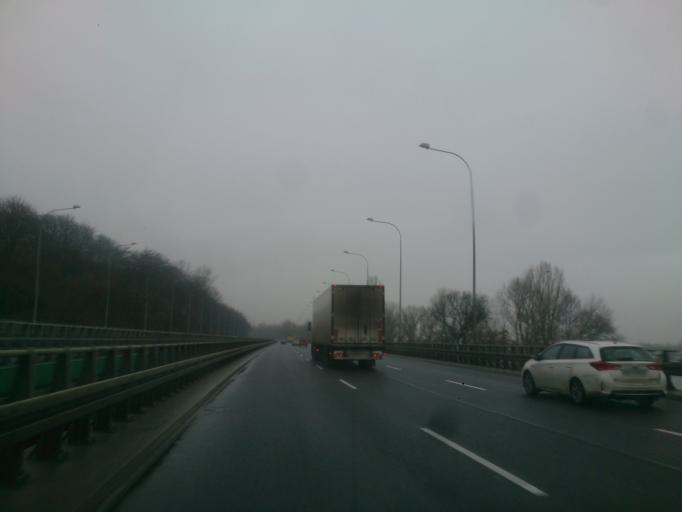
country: PL
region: Masovian Voivodeship
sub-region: Warszawa
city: Bialoleka
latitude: 52.2965
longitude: 20.9630
